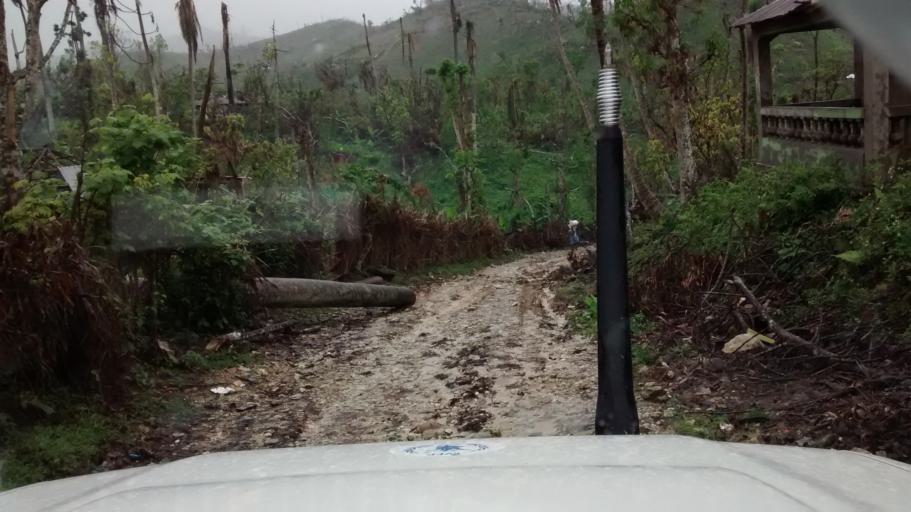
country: HT
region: Grandans
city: Moron
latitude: 18.5354
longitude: -74.1557
